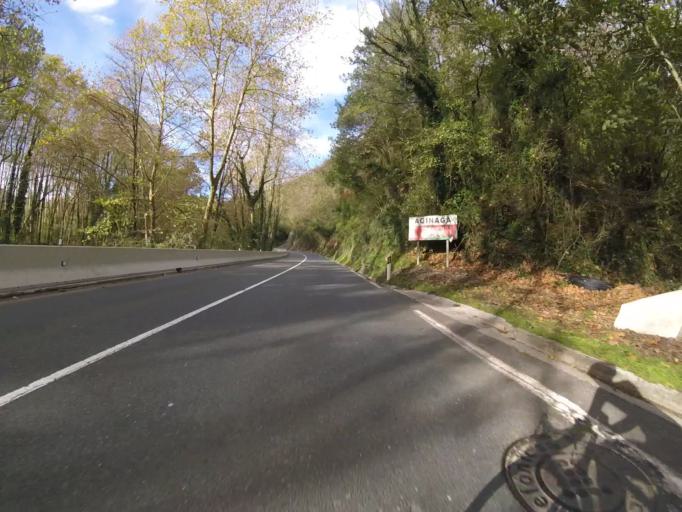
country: ES
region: Basque Country
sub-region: Provincia de Guipuzcoa
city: Usurbil
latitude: 43.2791
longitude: -2.0619
